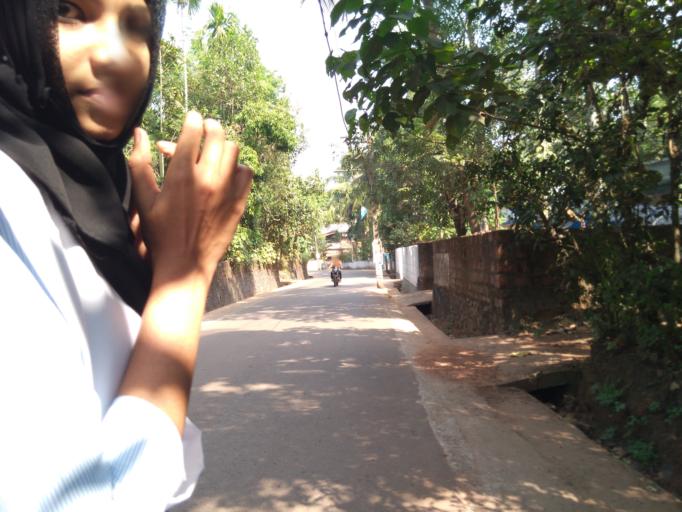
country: IN
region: Kerala
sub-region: Kozhikode
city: Kunnamangalam
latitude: 11.2927
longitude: 75.8368
